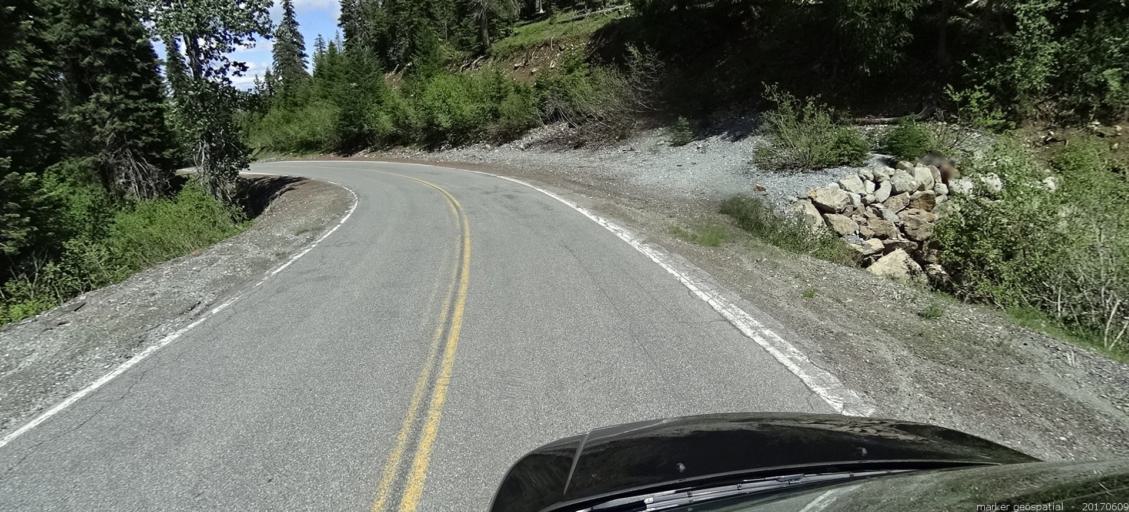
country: US
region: California
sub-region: Siskiyou County
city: Yreka
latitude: 41.4026
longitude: -122.9843
